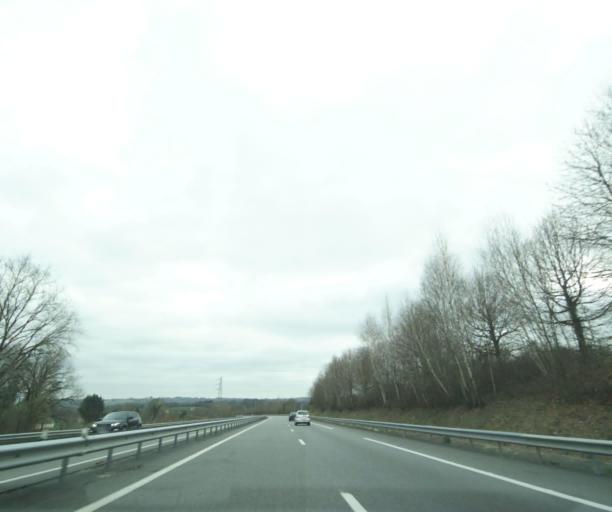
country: FR
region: Limousin
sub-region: Departement de la Correze
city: Uzerche
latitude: 45.5119
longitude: 1.5152
